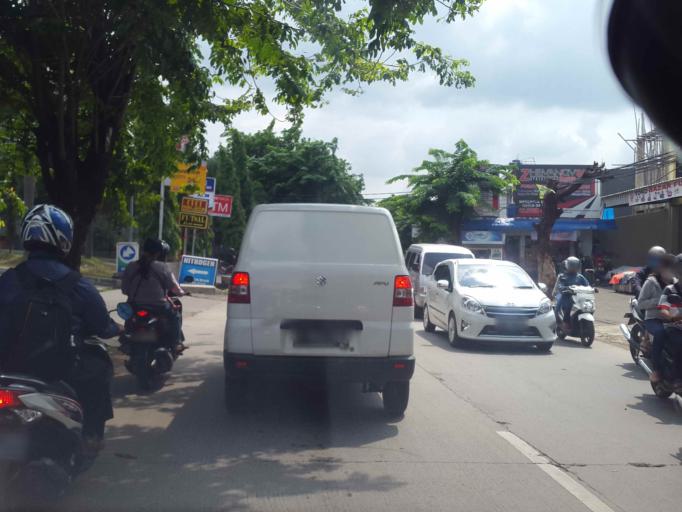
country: ID
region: West Java
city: Bekasi
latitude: -6.2868
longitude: 106.9679
